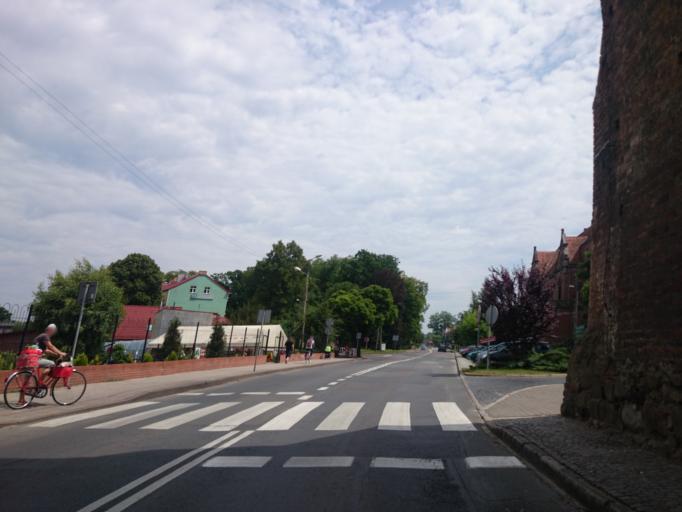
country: PL
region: West Pomeranian Voivodeship
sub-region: Powiat gryfinski
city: Chojna
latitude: 52.9609
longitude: 14.4326
